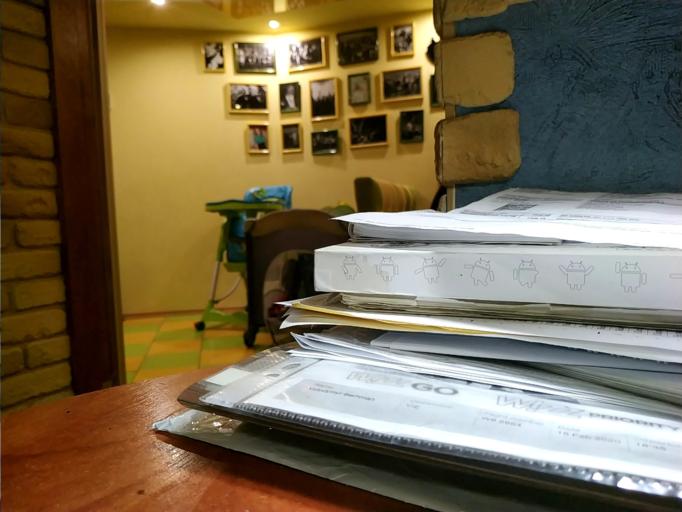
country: RU
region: Arkhangelskaya
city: Kargopol'
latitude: 61.4156
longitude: 39.3730
